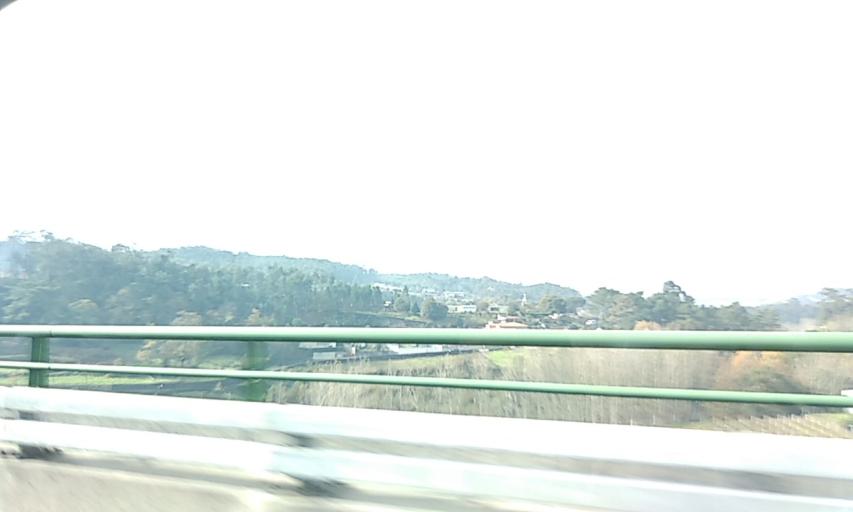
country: PT
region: Braga
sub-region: Braga
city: Oliveira
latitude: 41.5012
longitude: -8.4720
